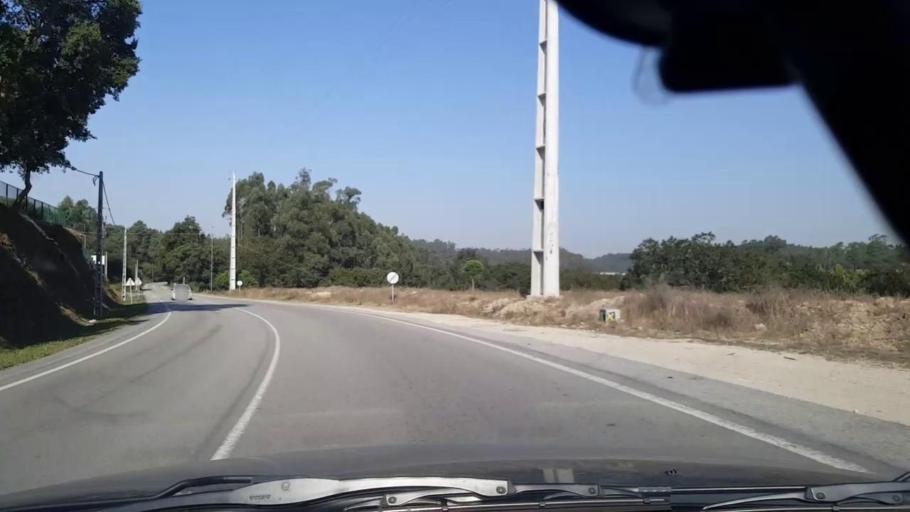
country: PT
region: Porto
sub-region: Vila do Conde
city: Arvore
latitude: 41.3487
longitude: -8.6790
